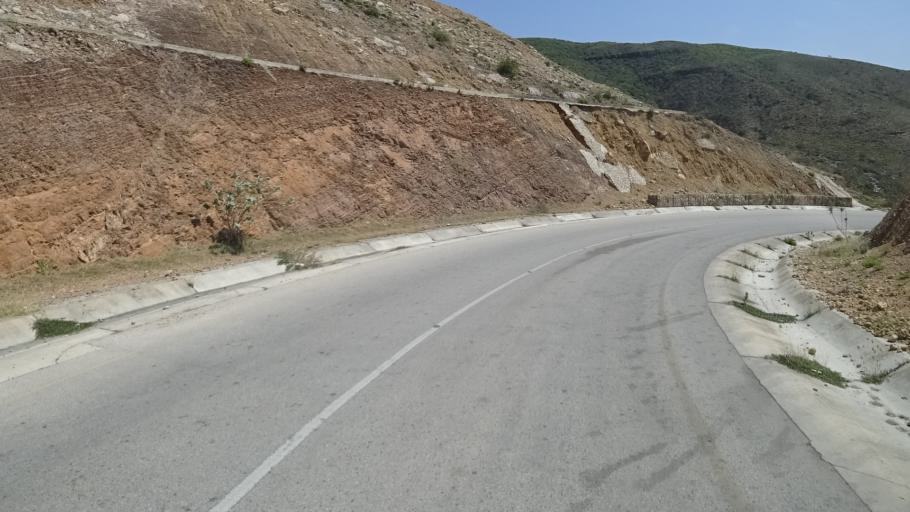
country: OM
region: Zufar
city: Salalah
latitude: 17.0470
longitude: 54.6128
